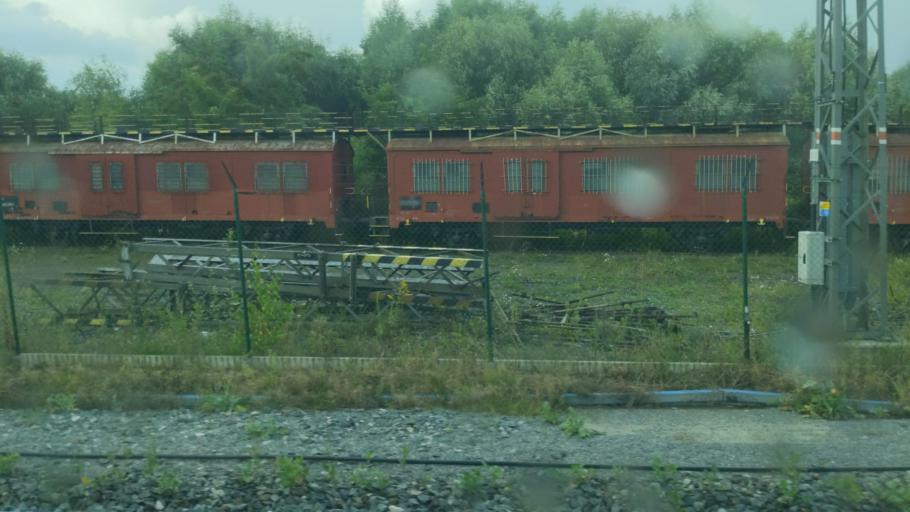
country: CZ
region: Central Bohemia
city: Poricany
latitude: 50.1112
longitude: 14.9312
